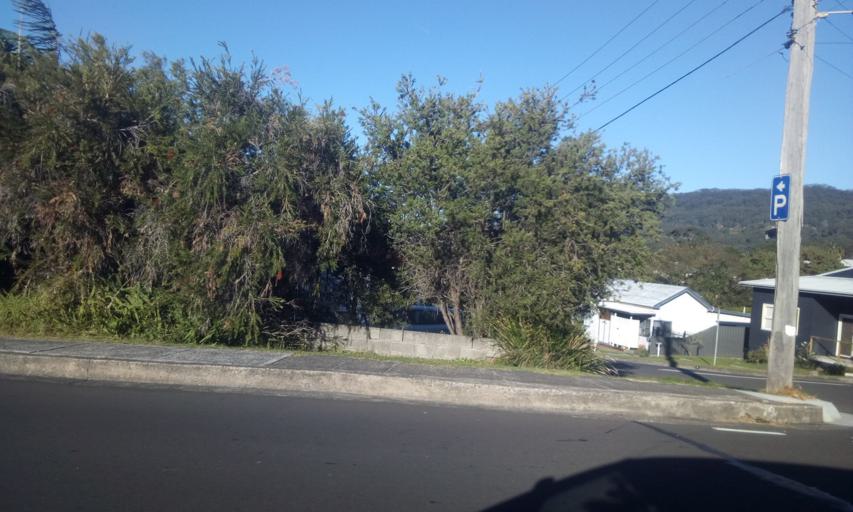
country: AU
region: New South Wales
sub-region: Wollongong
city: Bulli
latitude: -34.3403
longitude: 150.9057
